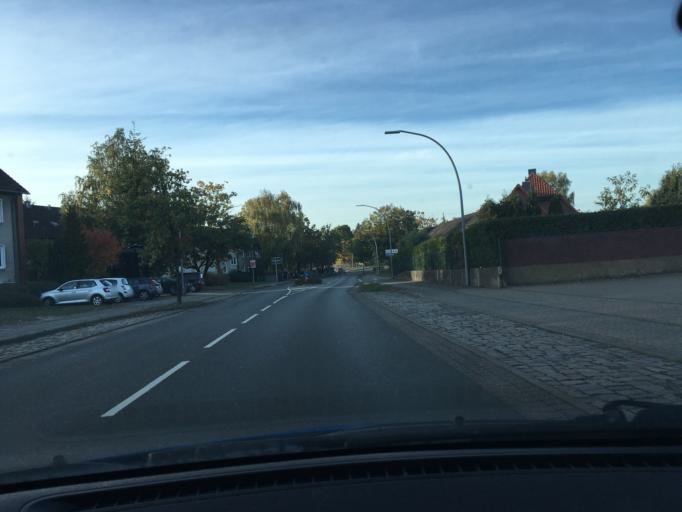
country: DE
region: Lower Saxony
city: Munster
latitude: 52.9875
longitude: 10.0833
